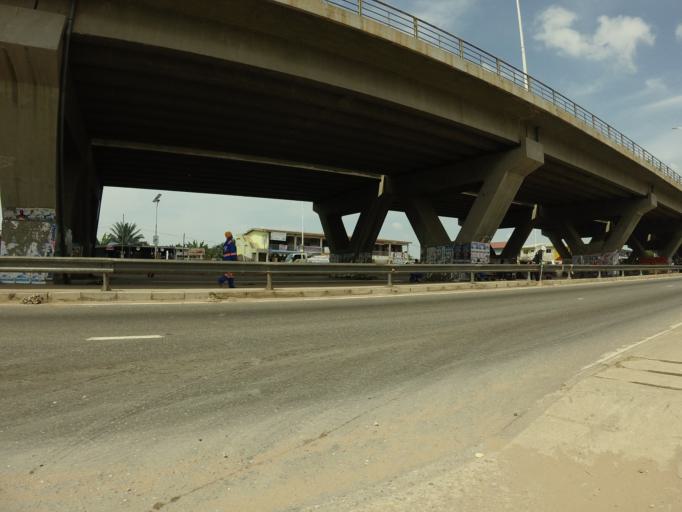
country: GH
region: Greater Accra
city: Dome
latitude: 5.6339
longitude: -0.2393
